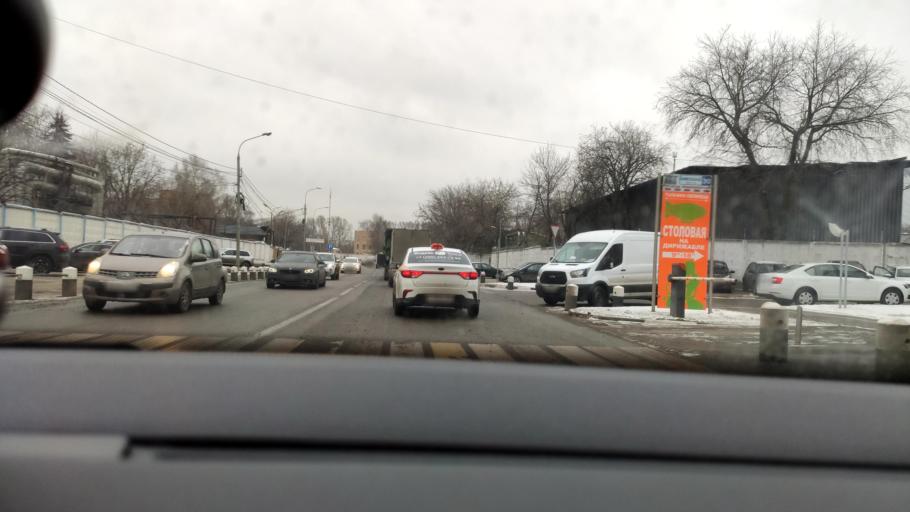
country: RU
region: Moscow
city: Khimki
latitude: 55.9115
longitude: 37.4196
